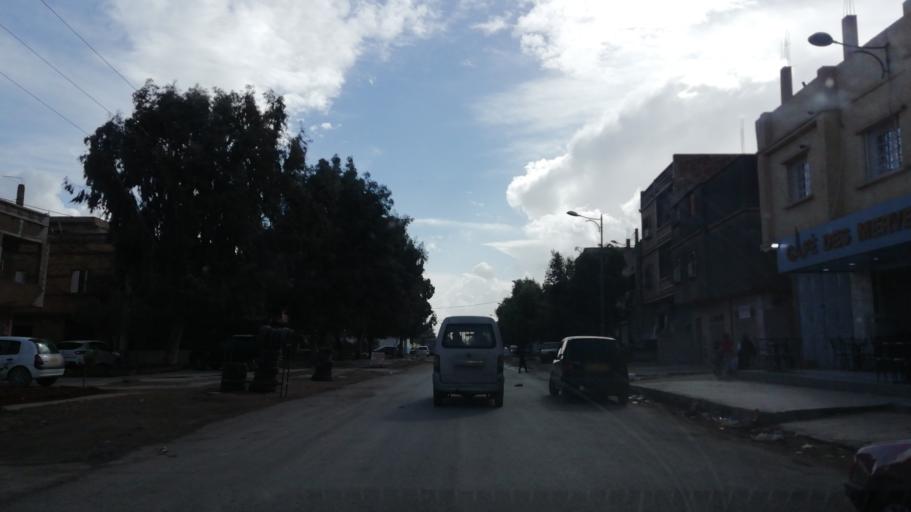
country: DZ
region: Oran
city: Sidi ech Chahmi
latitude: 35.6512
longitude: -0.5661
